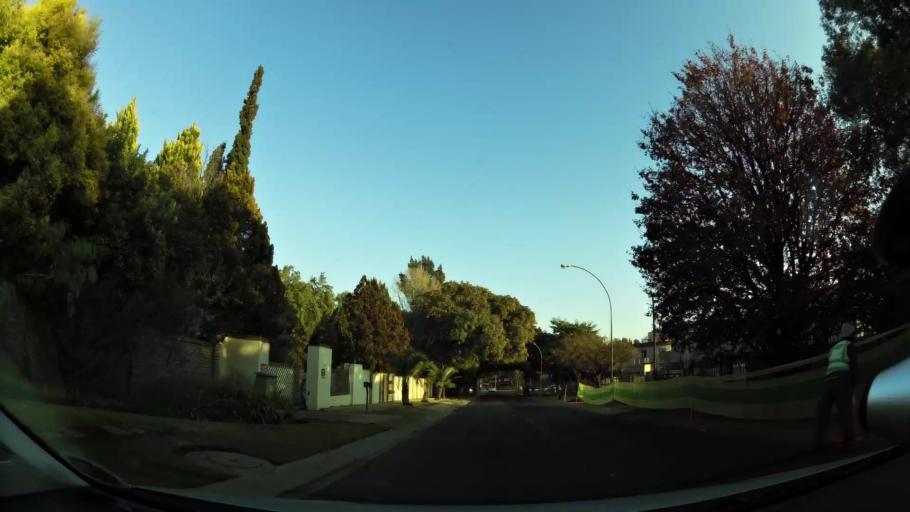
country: ZA
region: Orange Free State
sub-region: Mangaung Metropolitan Municipality
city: Bloemfontein
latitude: -29.0835
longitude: 26.1590
